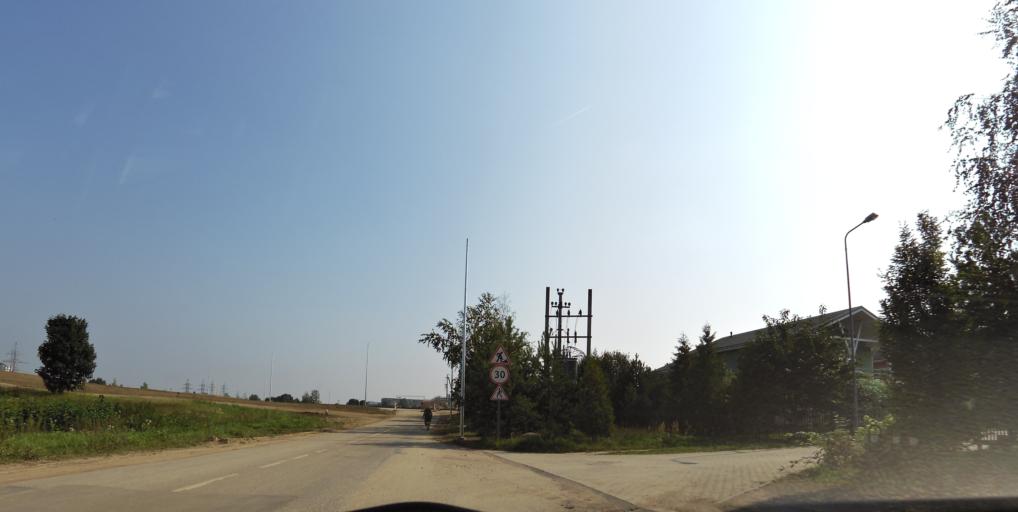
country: LT
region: Vilnius County
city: Justiniskes
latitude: 54.7248
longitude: 25.2047
